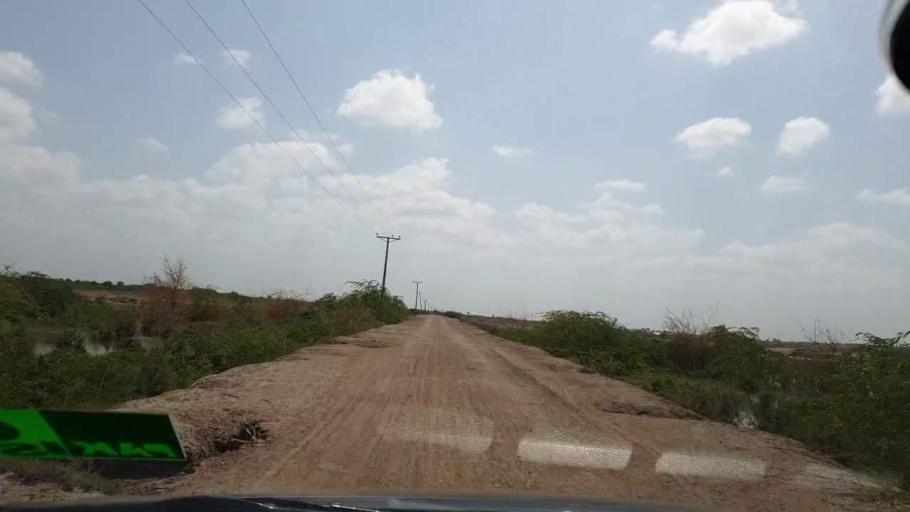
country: PK
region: Sindh
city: Kadhan
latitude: 24.6067
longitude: 69.1852
